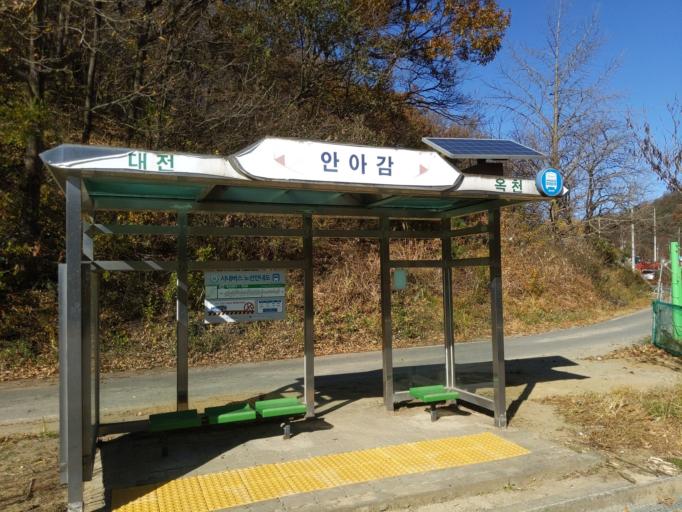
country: KR
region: Chungcheongbuk-do
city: Okcheon
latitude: 36.3533
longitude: 127.5160
